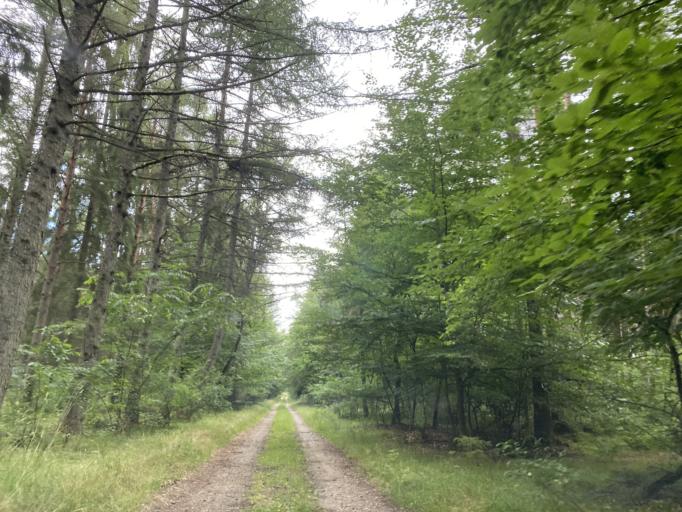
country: DK
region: Central Jutland
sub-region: Viborg Kommune
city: Bjerringbro
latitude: 56.2654
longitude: 9.6466
